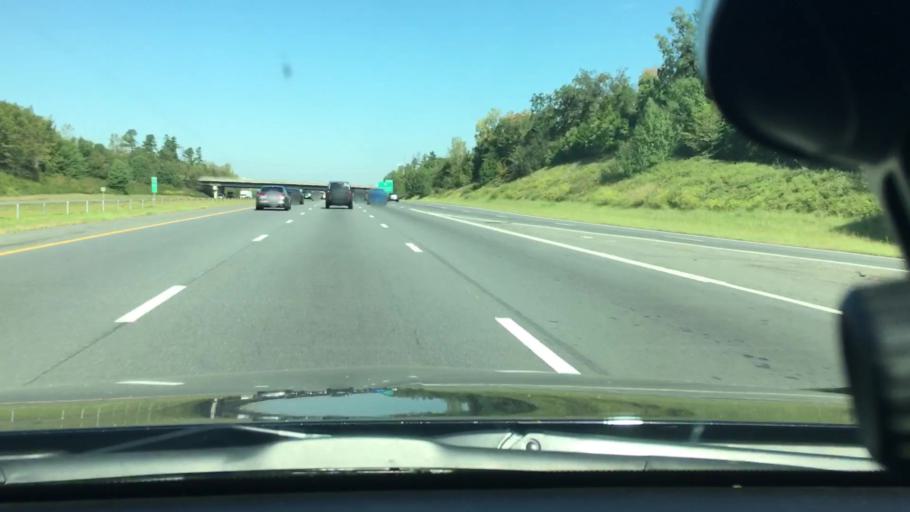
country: US
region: North Carolina
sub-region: Cabarrus County
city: Harrisburg
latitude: 35.3165
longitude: -80.7104
